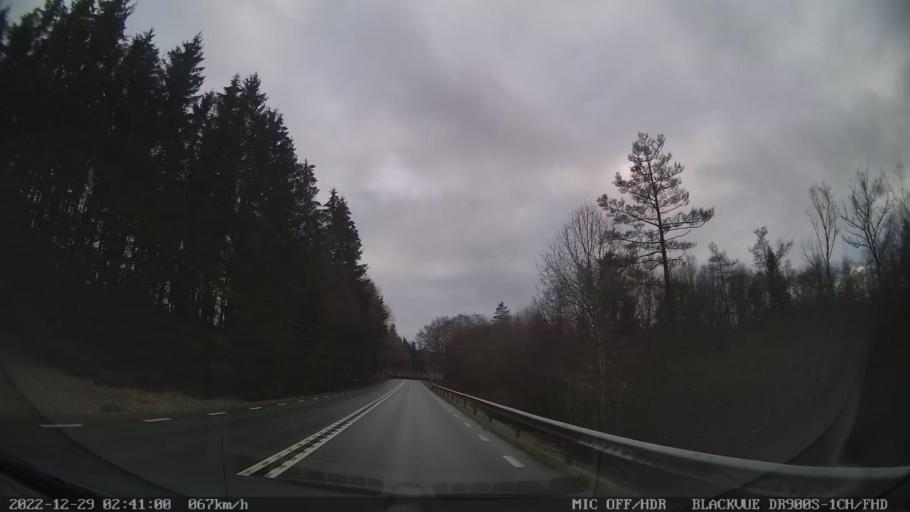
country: SE
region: Skane
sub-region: Simrishamns Kommun
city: Kivik
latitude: 55.6093
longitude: 14.1414
